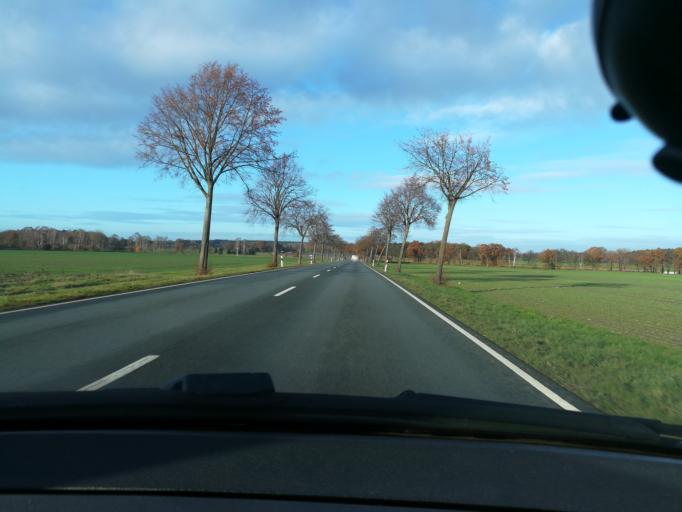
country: DE
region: Lower Saxony
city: Uchte
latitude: 52.5125
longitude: 8.9020
